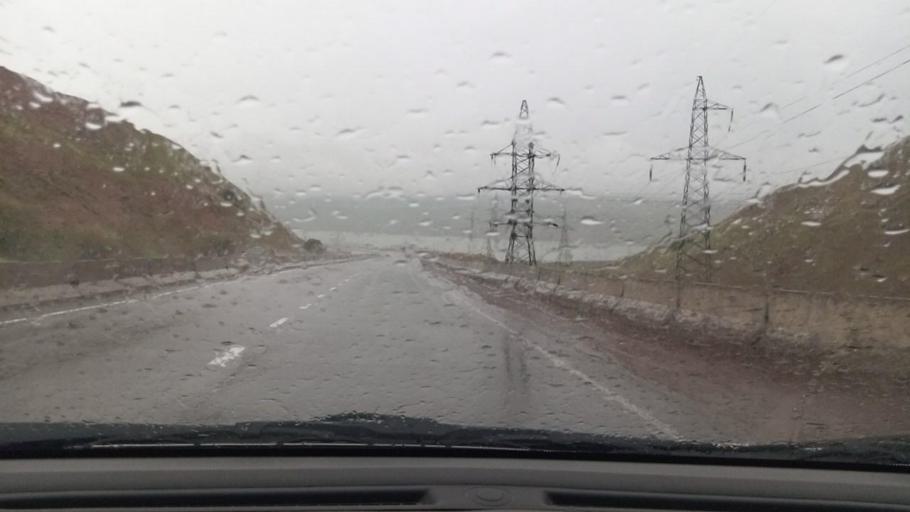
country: UZ
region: Toshkent
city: Angren
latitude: 41.0602
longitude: 70.1926
